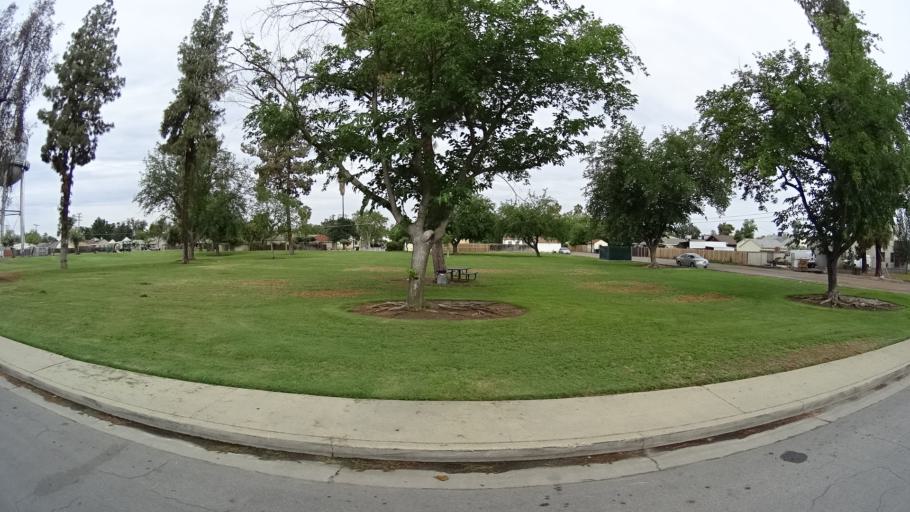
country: US
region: California
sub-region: Kings County
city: Hanford
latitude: 36.3420
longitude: -119.6427
